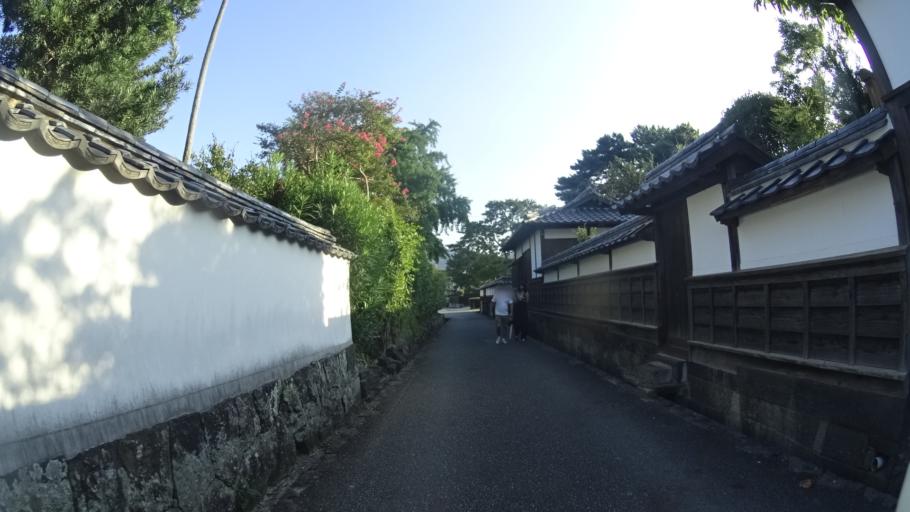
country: JP
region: Yamaguchi
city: Hagi
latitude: 34.4120
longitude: 131.3948
